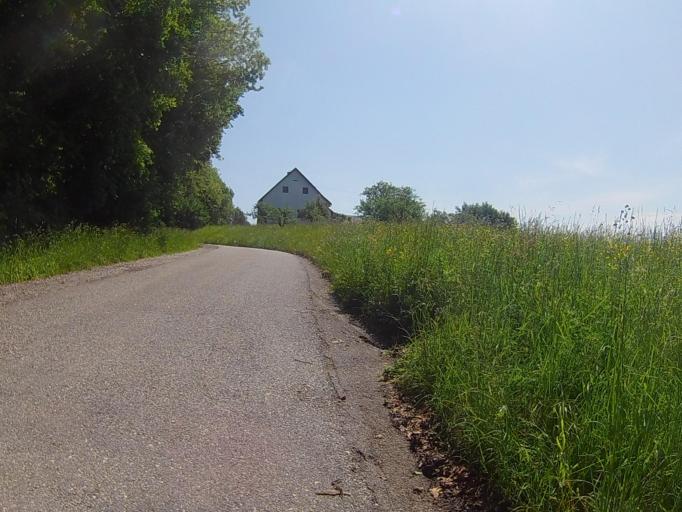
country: SI
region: Pesnica
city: Pesnica pri Mariboru
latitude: 46.5710
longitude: 15.7049
